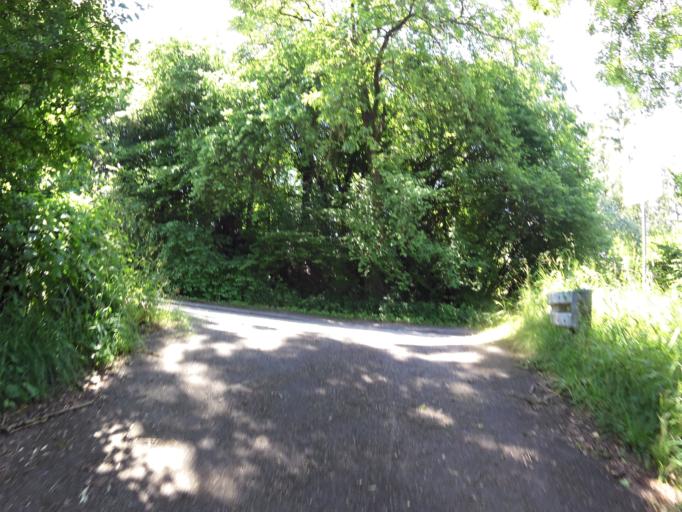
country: DE
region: Baden-Wuerttemberg
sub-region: Freiburg Region
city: Lahr
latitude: 48.3257
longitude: 7.8612
